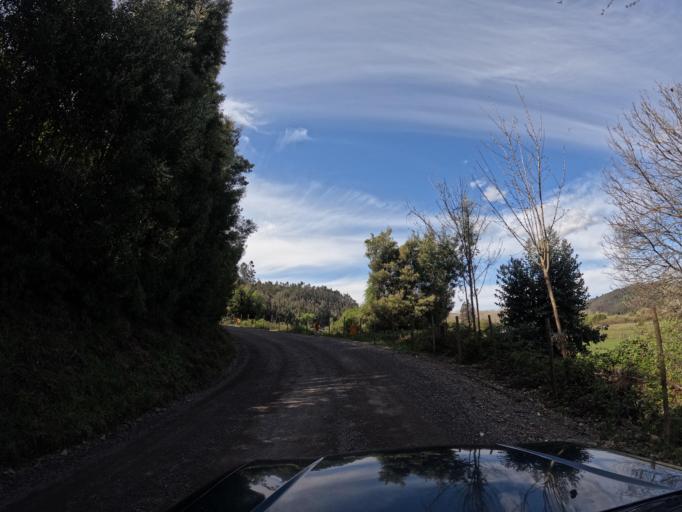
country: CL
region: Biobio
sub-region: Provincia de Concepcion
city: Chiguayante
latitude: -37.0714
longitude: -72.9060
